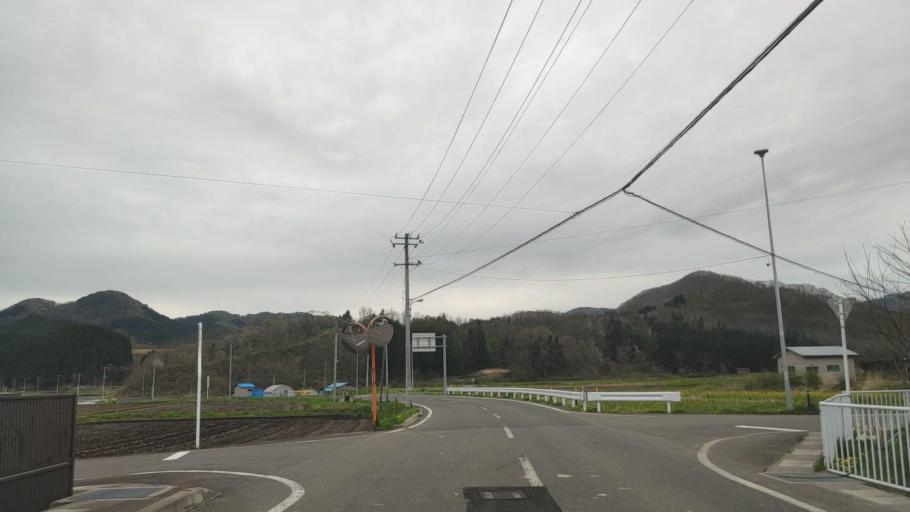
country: JP
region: Akita
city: Odate
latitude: 40.3703
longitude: 140.7270
